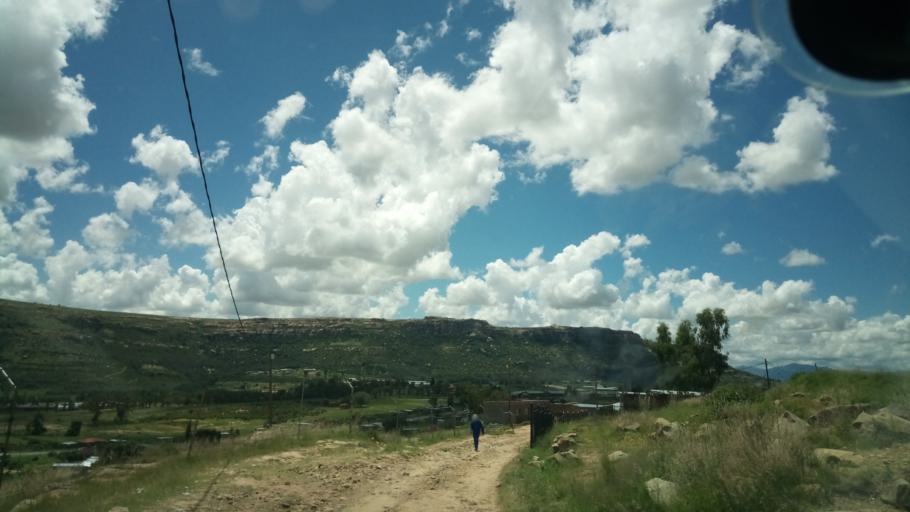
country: LS
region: Maseru
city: Maseru
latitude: -29.3509
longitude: 27.5279
